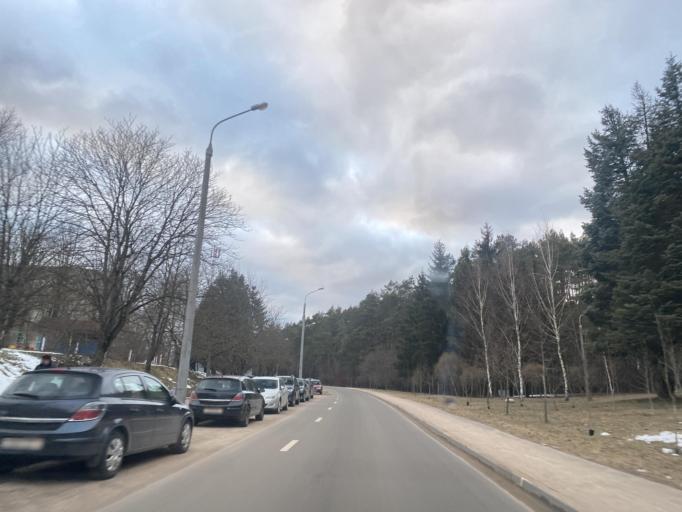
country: BY
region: Minsk
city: Borovlyany
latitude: 53.9521
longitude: 27.6410
